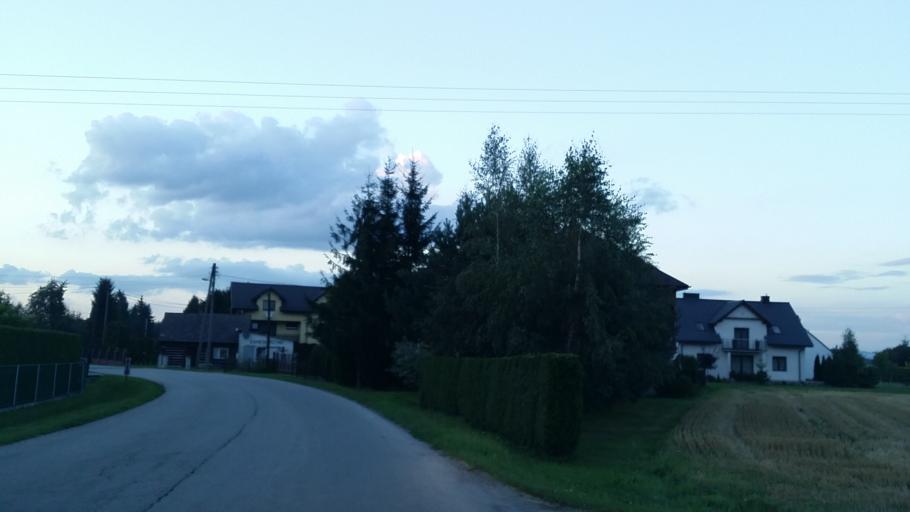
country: PL
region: Lesser Poland Voivodeship
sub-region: Powiat oswiecimski
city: Przeciszow
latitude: 50.0122
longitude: 19.3736
